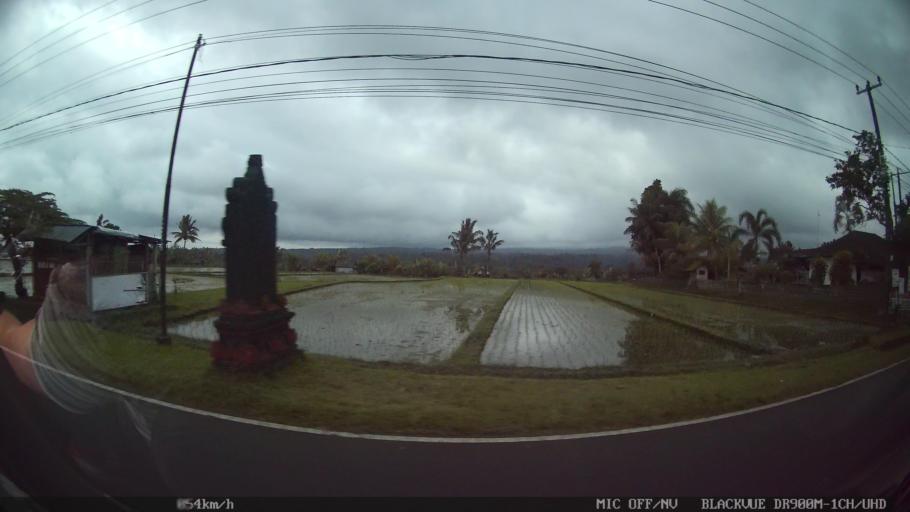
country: ID
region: Bali
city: Empalan
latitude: -8.4033
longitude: 115.1473
